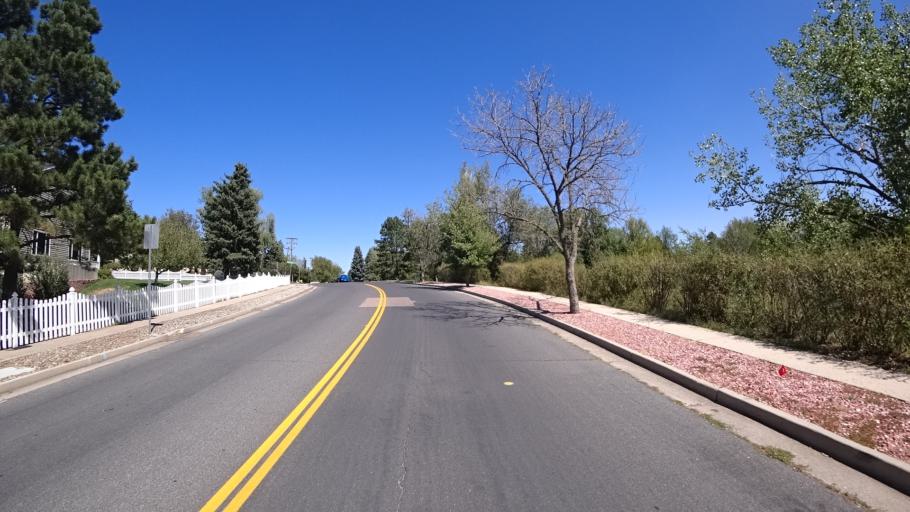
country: US
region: Colorado
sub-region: El Paso County
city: Colorado Springs
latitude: 38.7933
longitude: -104.8333
